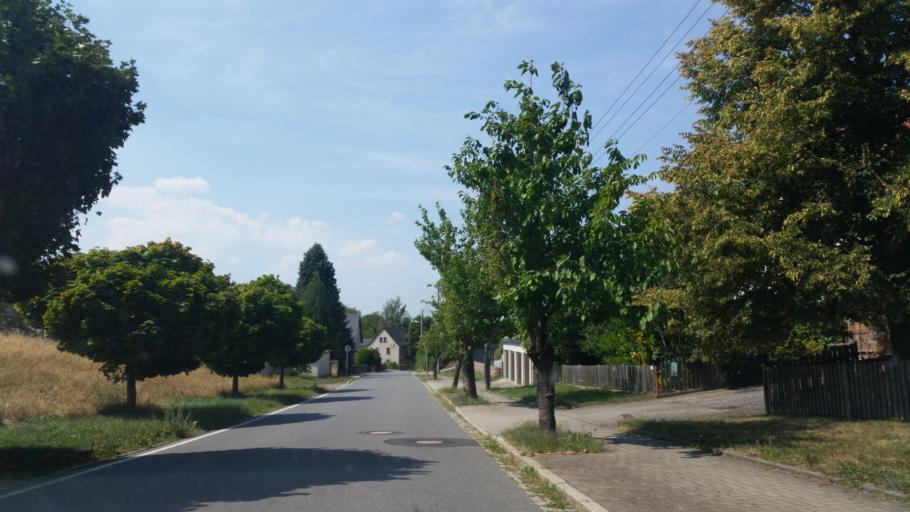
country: DE
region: Saxony
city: Wilsdruff
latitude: 51.0680
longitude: 13.5412
